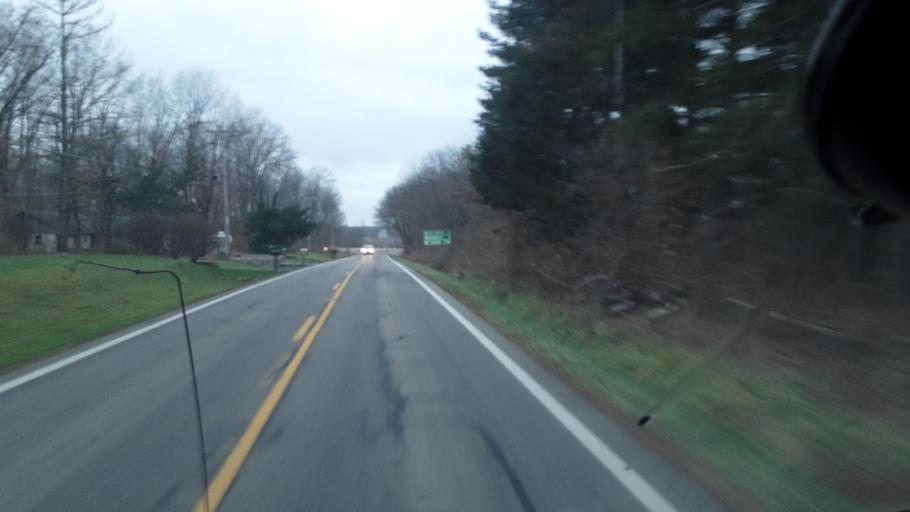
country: US
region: Ohio
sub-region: Delaware County
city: Sunbury
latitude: 40.3197
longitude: -82.8403
